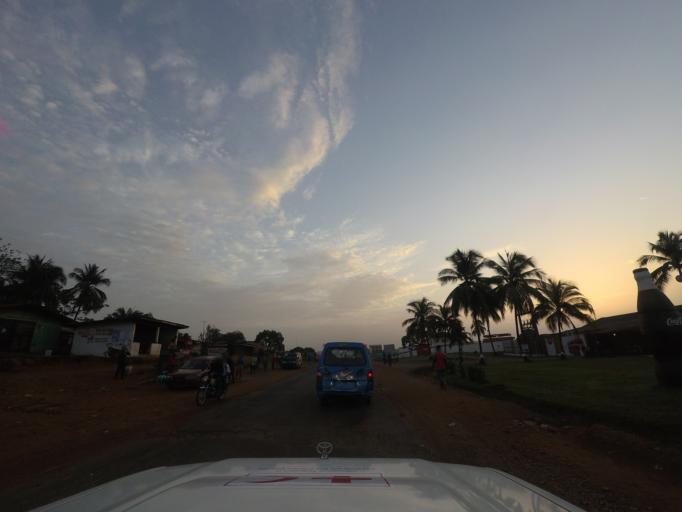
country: LR
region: Montserrado
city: Monrovia
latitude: 6.3013
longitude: -10.6774
